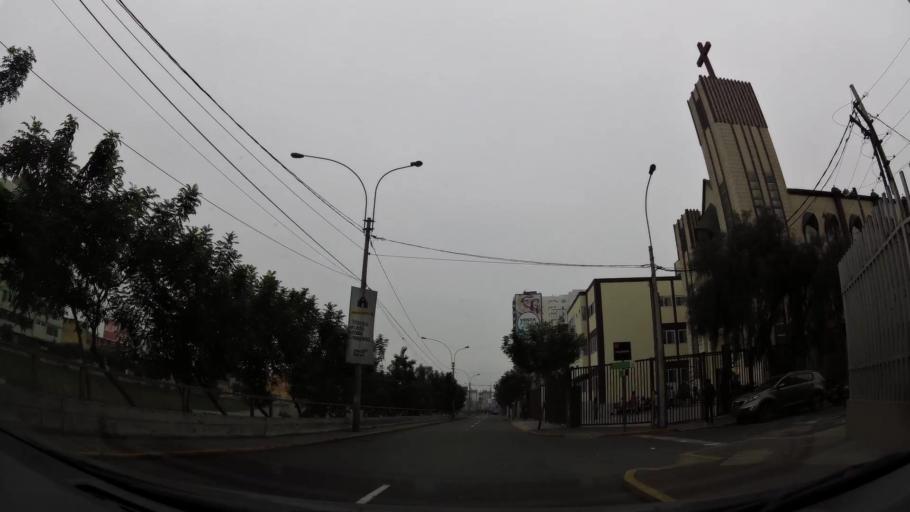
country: PE
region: Lima
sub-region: Lima
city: San Isidro
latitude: -12.1093
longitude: -77.0267
